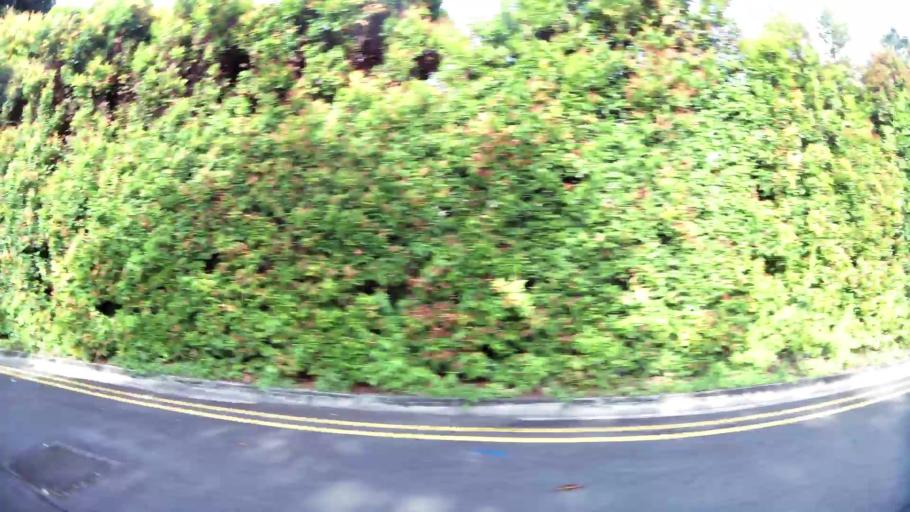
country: SG
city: Singapore
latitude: 1.2527
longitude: 103.8187
